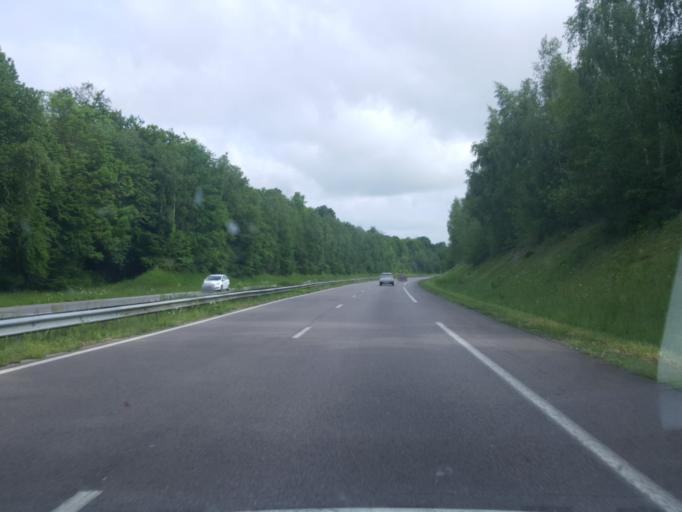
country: FR
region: Haute-Normandie
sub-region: Departement de l'Eure
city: Heudreville-sur-Eure
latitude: 49.1067
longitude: 1.1877
